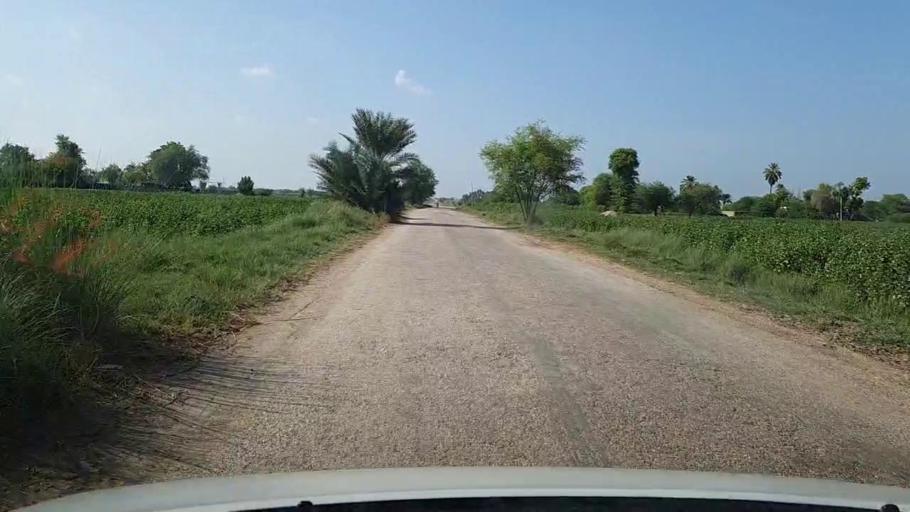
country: PK
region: Sindh
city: Kandiaro
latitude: 27.0584
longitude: 68.3168
